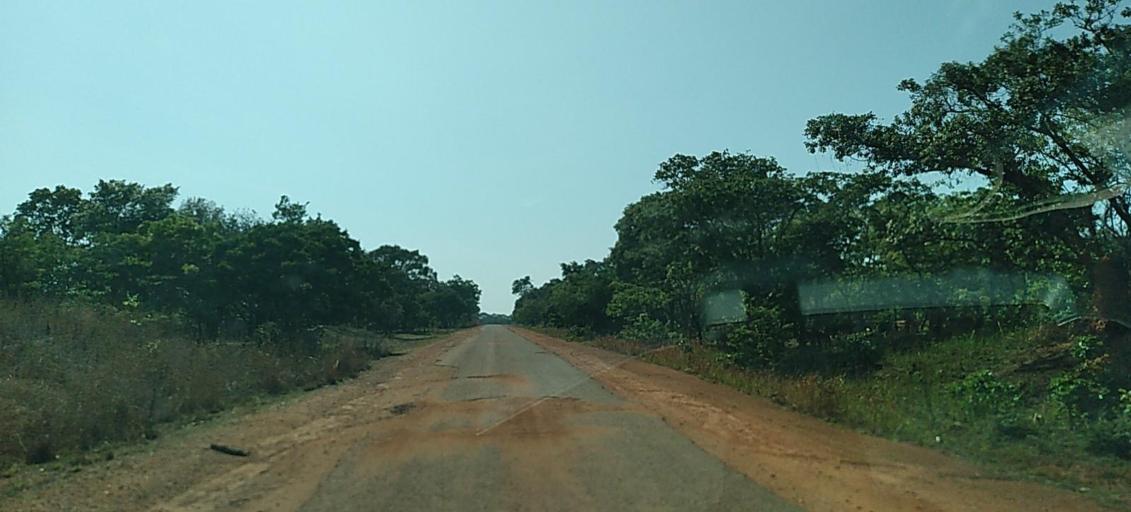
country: ZM
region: North-Western
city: Mwinilunga
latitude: -11.8906
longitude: 25.2623
